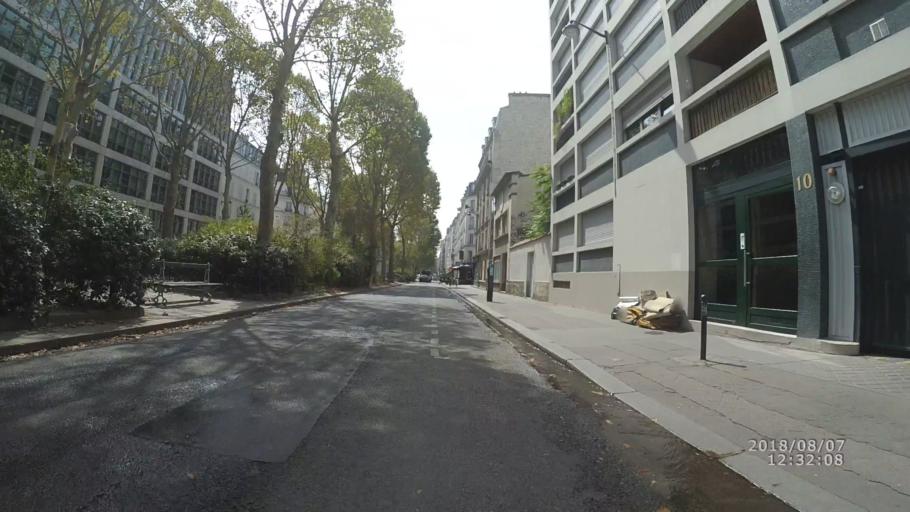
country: FR
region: Ile-de-France
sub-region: Departement du Val-de-Marne
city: Gentilly
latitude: 48.8313
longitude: 2.3334
